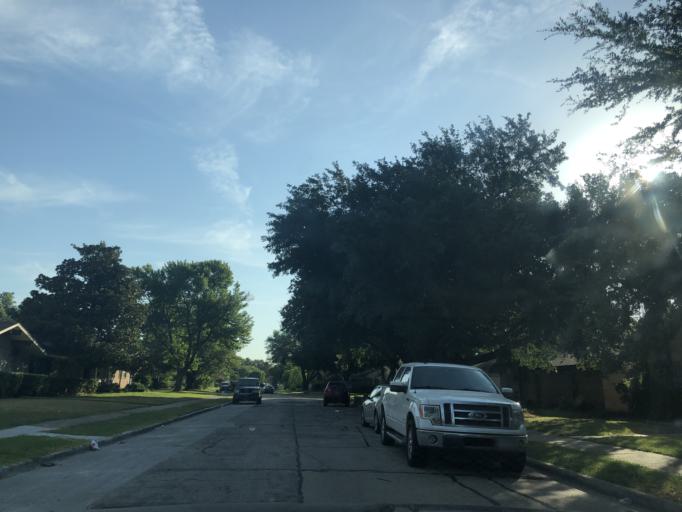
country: US
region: Texas
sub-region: Dallas County
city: Garland
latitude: 32.8474
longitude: -96.6355
